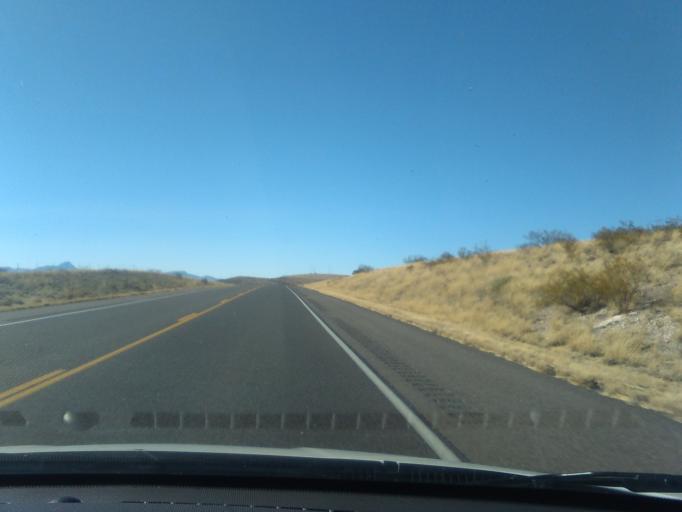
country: US
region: New Mexico
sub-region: Dona Ana County
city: Hatch
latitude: 32.5772
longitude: -107.4374
